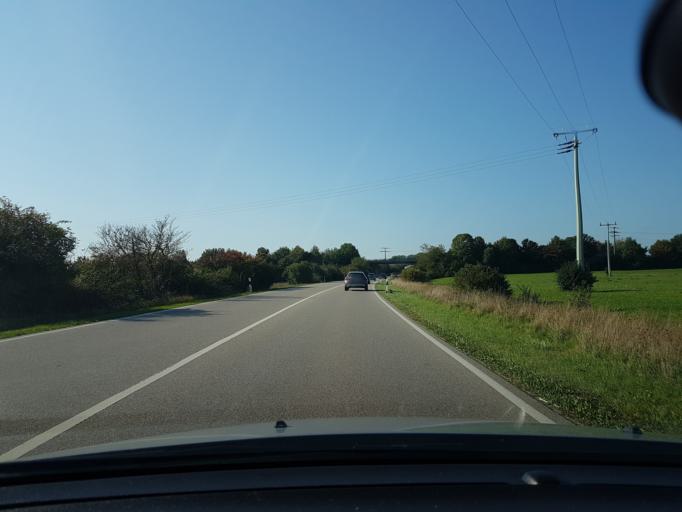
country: DE
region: Bavaria
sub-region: Upper Bavaria
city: Stammham
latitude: 48.2964
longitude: 11.8775
